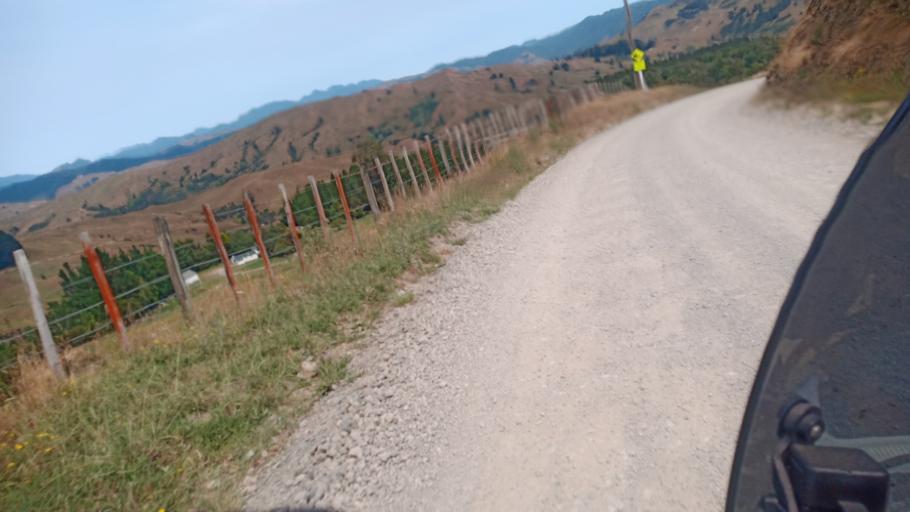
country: NZ
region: Bay of Plenty
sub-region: Opotiki District
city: Opotiki
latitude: -37.6573
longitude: 178.1218
